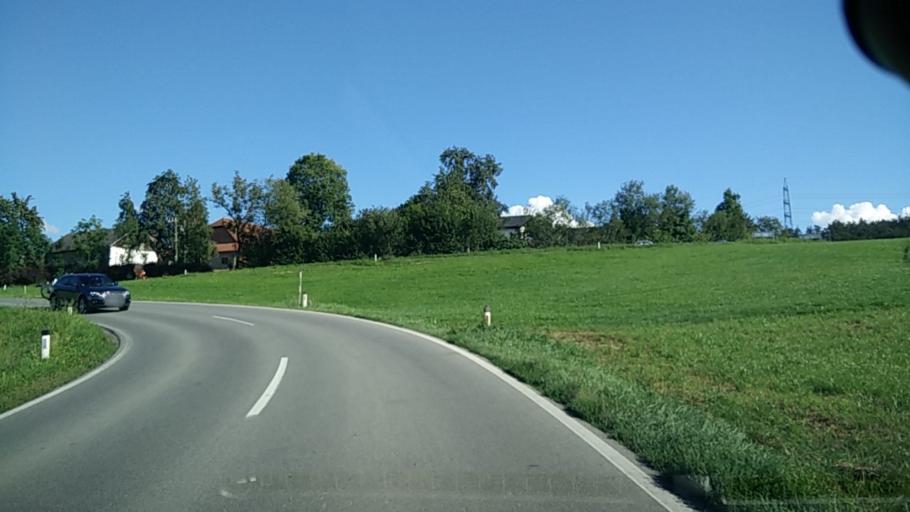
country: AT
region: Carinthia
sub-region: Politischer Bezirk Volkermarkt
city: Gallizien
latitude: 46.6193
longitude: 14.5583
